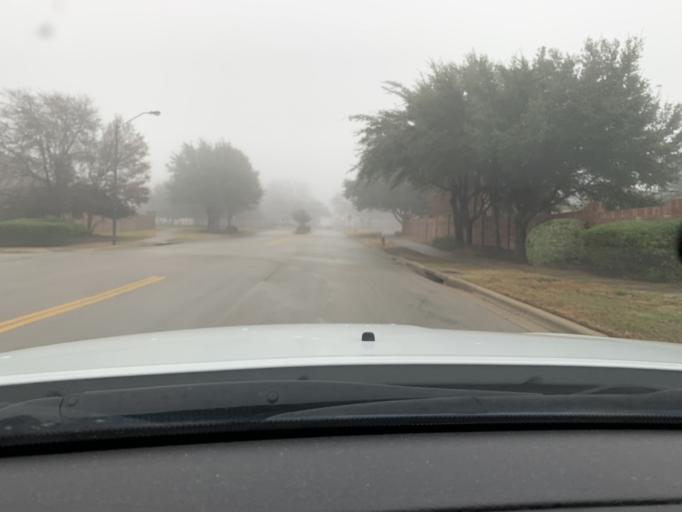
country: US
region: Texas
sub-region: Williamson County
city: Round Rock
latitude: 30.5703
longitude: -97.6728
